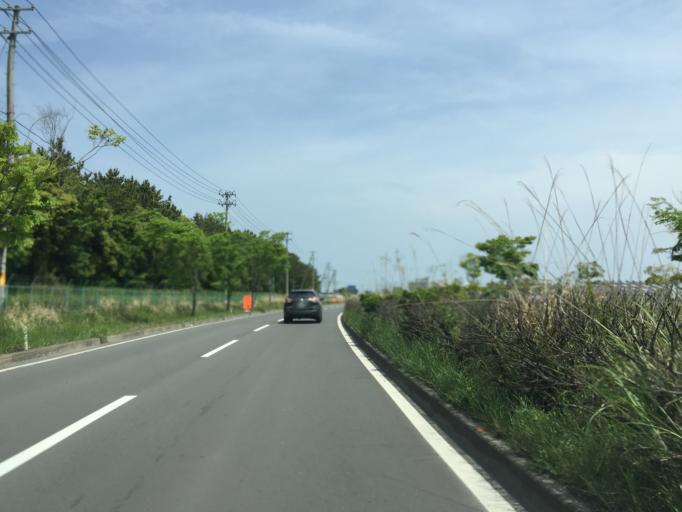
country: JP
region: Miyagi
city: Marumori
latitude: 37.8388
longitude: 140.9454
